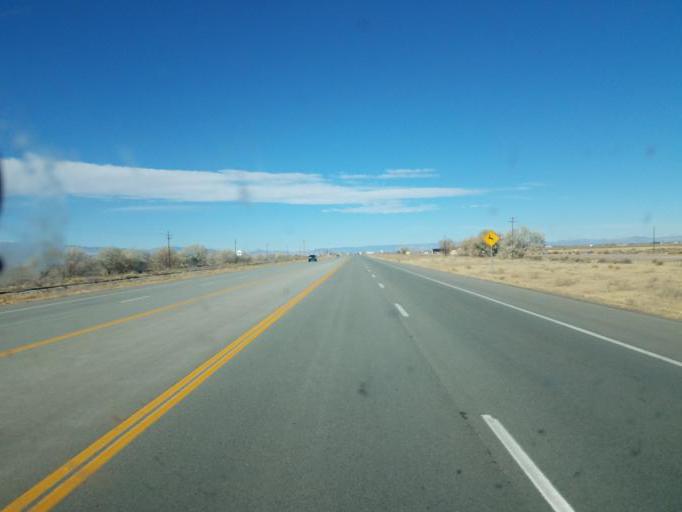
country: US
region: Colorado
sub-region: Alamosa County
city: Alamosa
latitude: 37.5184
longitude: -105.9963
